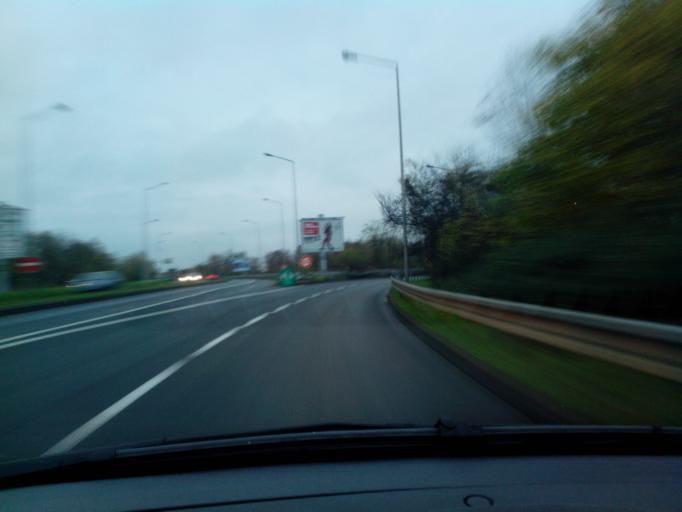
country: FR
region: Ile-de-France
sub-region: Departement de l'Essonne
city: Ris-Orangis
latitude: 48.6361
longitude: 2.4140
